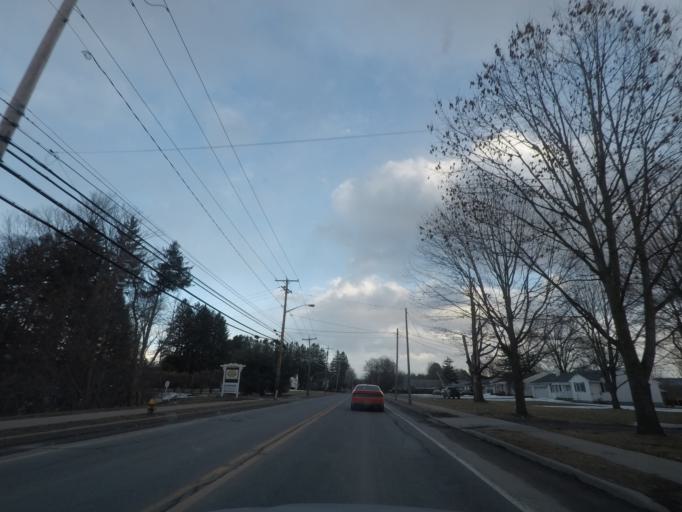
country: US
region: New York
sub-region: Oneida County
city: Utica
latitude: 43.1111
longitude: -75.1866
